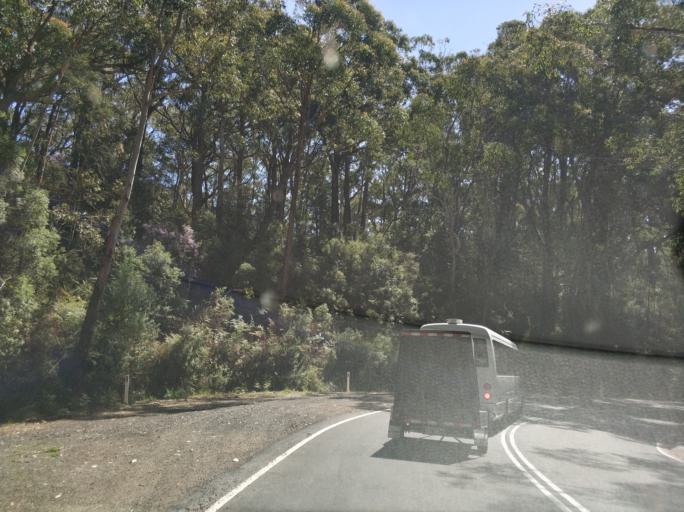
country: AU
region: Victoria
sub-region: Colac-Otway
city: Apollo Bay
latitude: -38.7451
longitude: 143.2574
